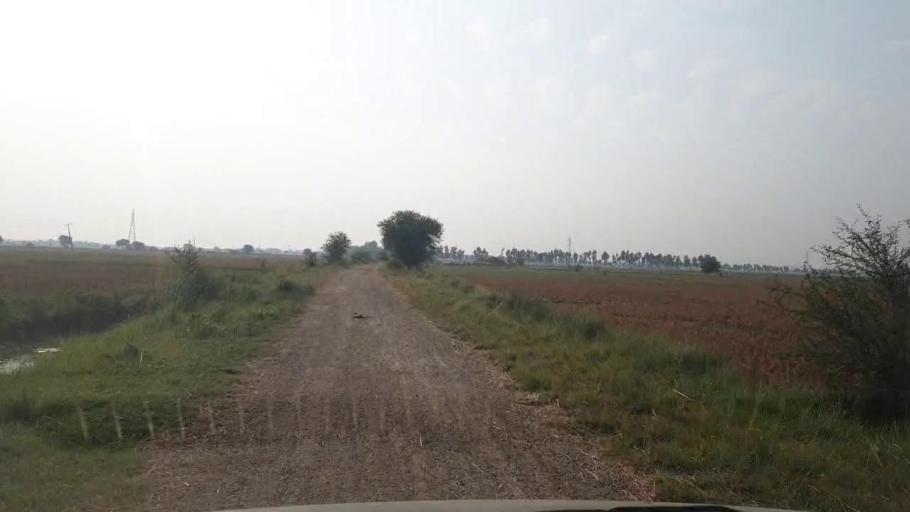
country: PK
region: Sindh
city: Tando Muhammad Khan
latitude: 25.1020
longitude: 68.5016
